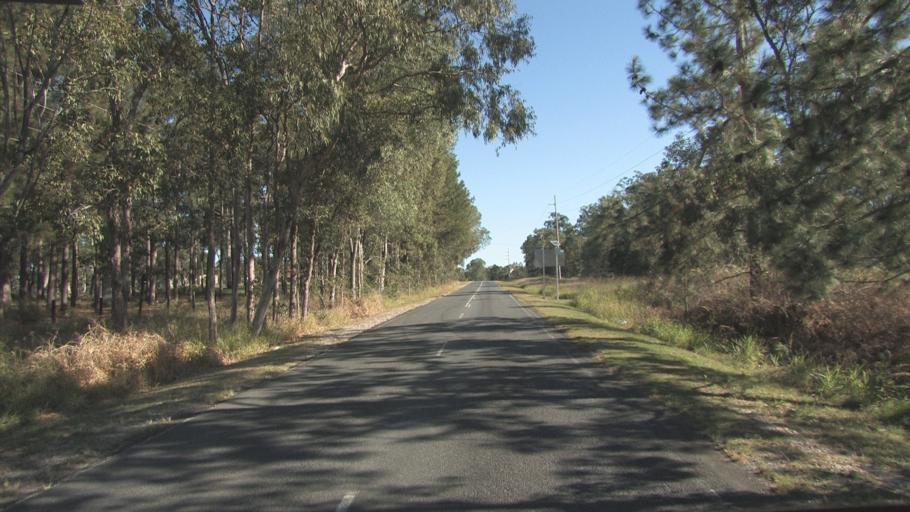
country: AU
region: Queensland
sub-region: Logan
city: North Maclean
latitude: -27.7865
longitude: 153.0473
